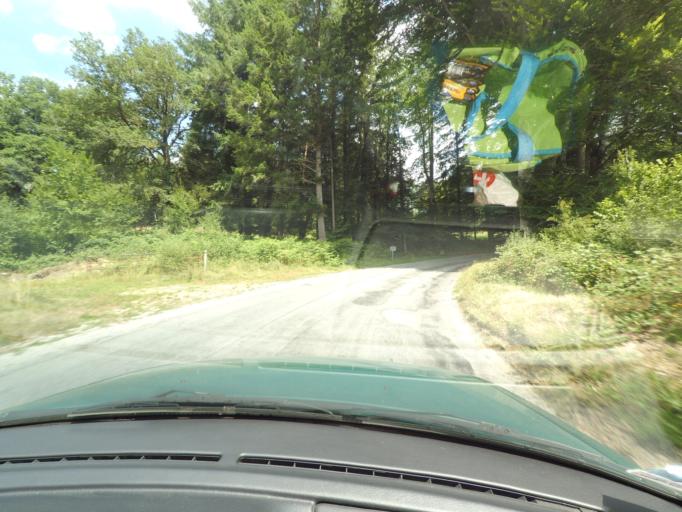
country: FR
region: Limousin
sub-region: Departement de la Correze
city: Bugeat
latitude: 45.7361
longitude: 1.8979
